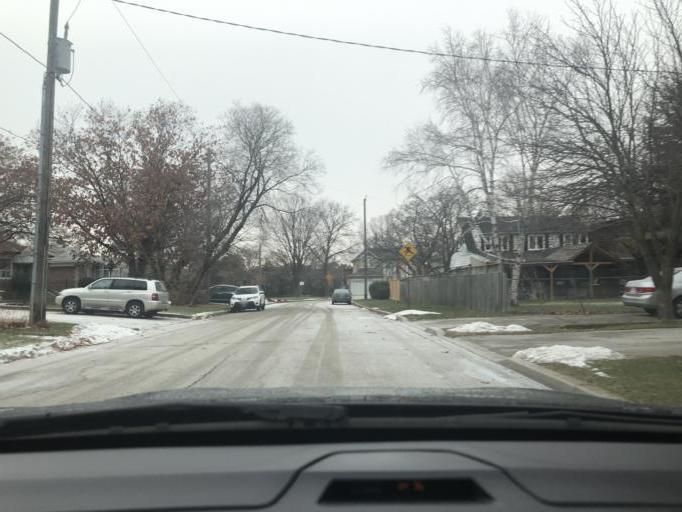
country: CA
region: Ontario
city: Scarborough
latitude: 43.7847
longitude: -79.2715
